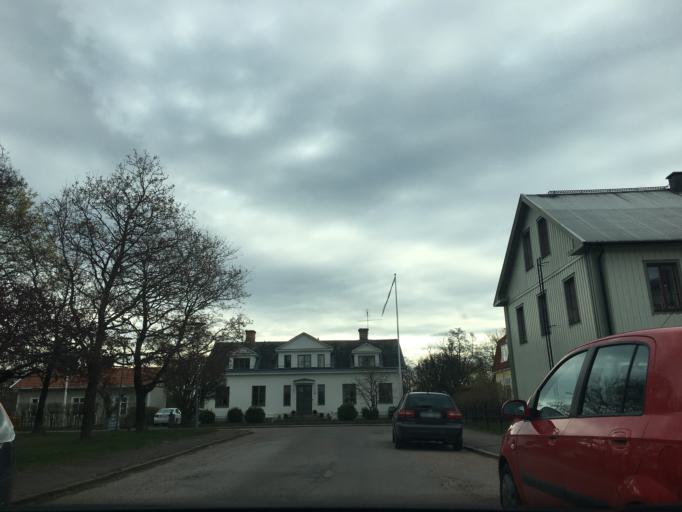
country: SE
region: Vaermland
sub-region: Kristinehamns Kommun
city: Kristinehamn
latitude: 59.3137
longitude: 14.1100
